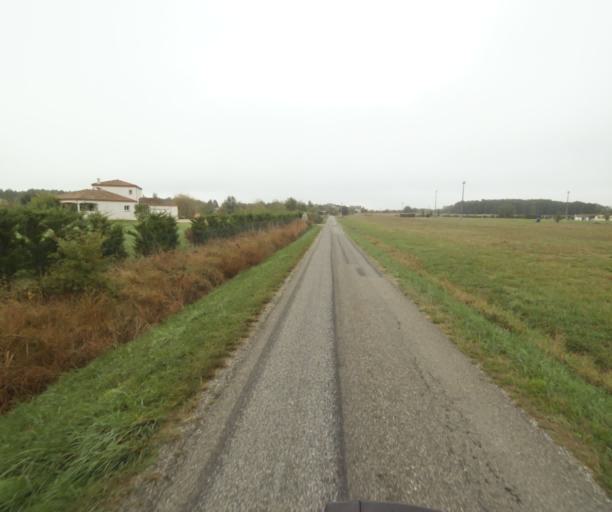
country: FR
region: Midi-Pyrenees
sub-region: Departement du Tarn-et-Garonne
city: Orgueil
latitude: 43.9047
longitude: 1.4005
